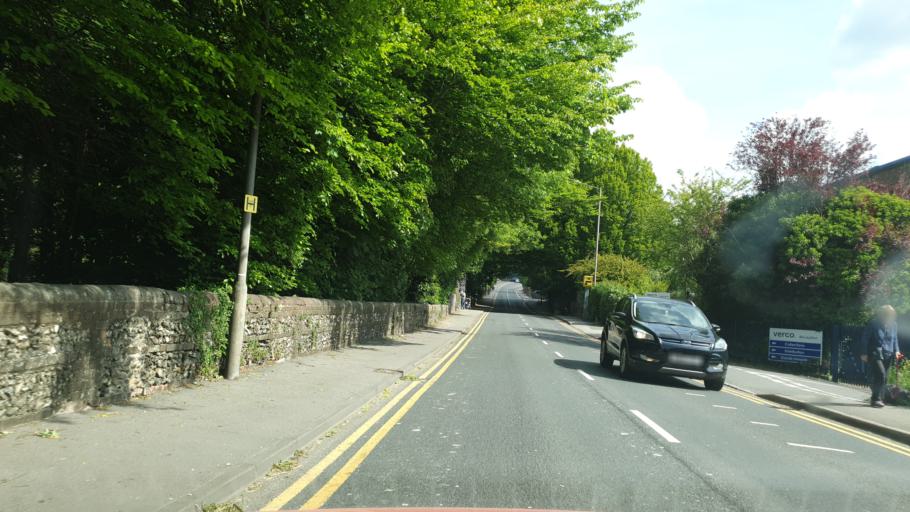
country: GB
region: England
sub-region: Buckinghamshire
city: High Wycombe
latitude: 51.6380
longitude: -0.7839
